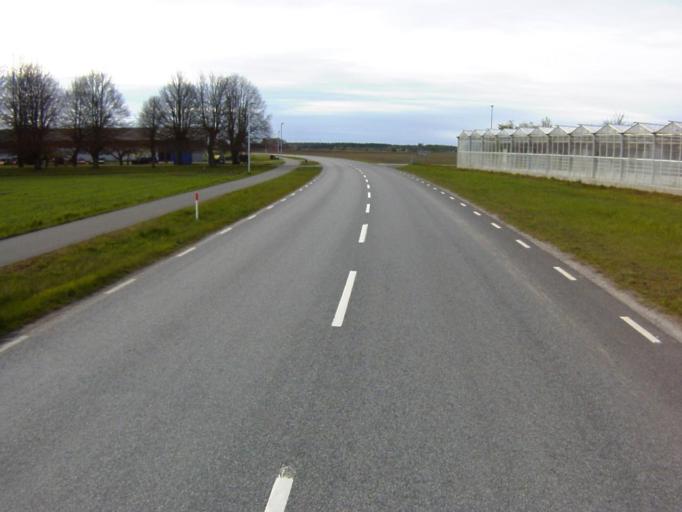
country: SE
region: Skane
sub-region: Kristianstads Kommun
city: Kristianstad
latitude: 56.0108
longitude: 14.1256
